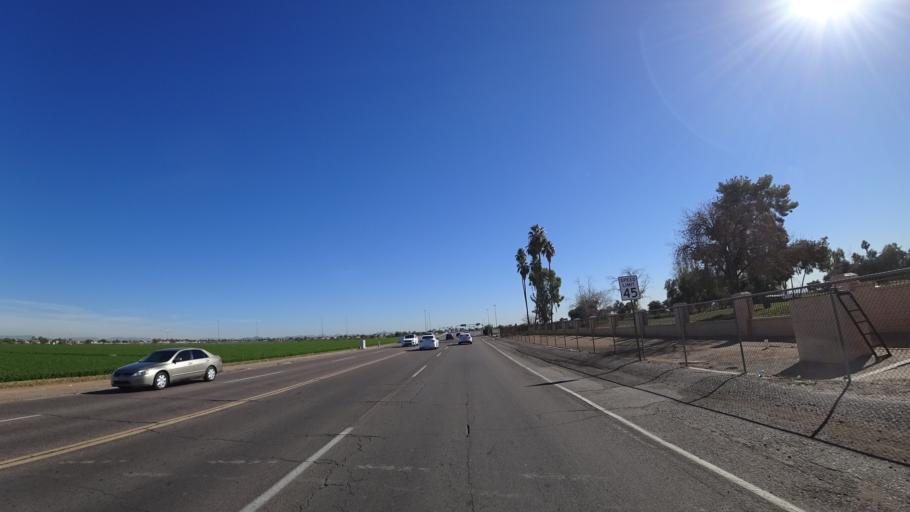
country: US
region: Arizona
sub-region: Maricopa County
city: Tolleson
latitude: 33.4938
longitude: -112.2690
